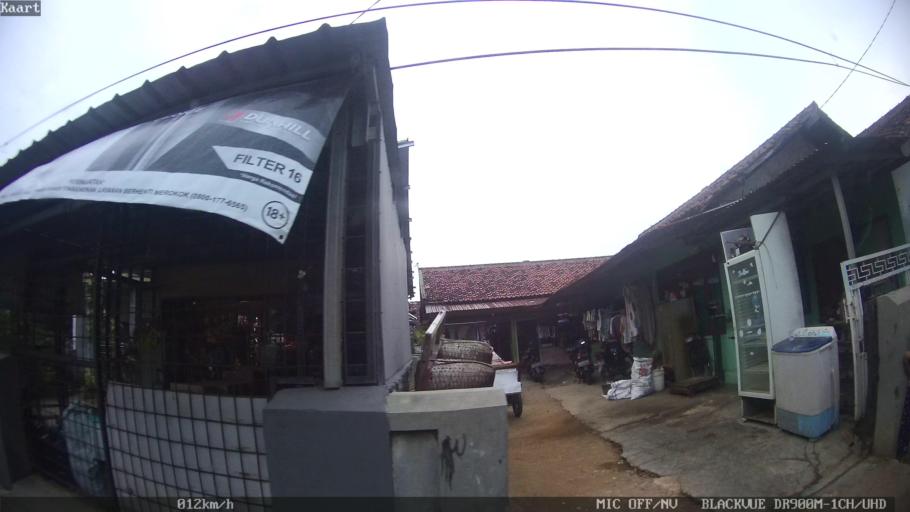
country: ID
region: Lampung
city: Kedaton
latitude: -5.4006
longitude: 105.2676
